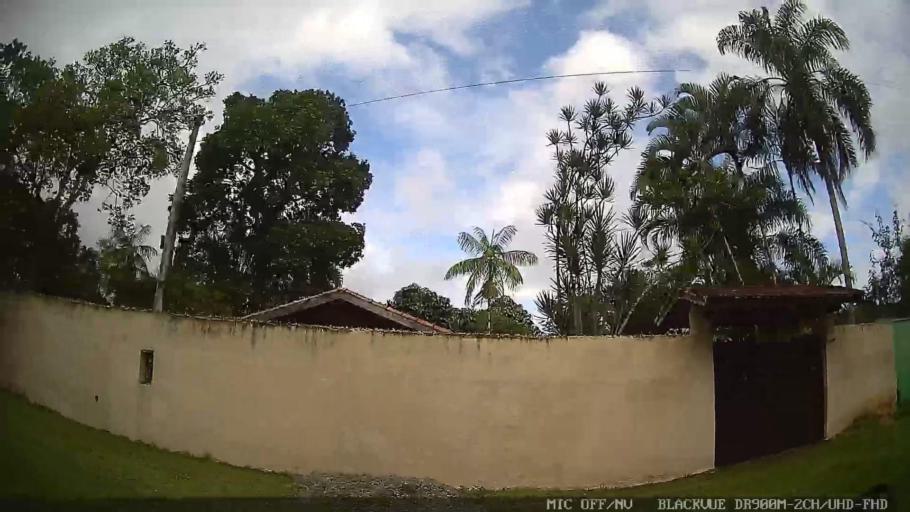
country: BR
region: Sao Paulo
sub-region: Itanhaem
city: Itanhaem
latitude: -24.2109
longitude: -46.8900
